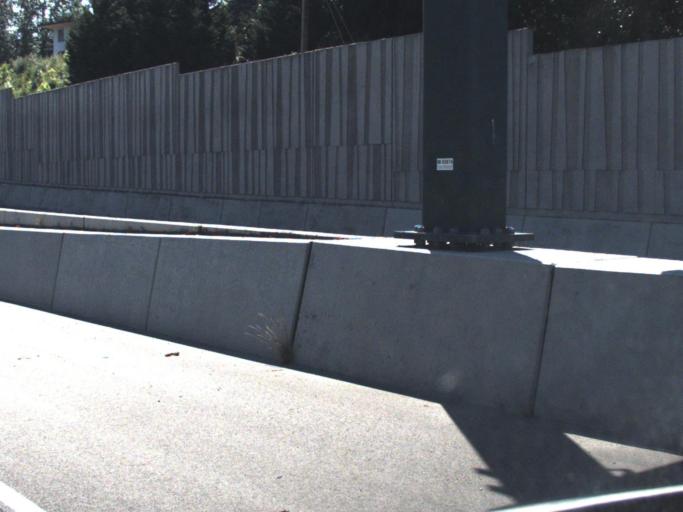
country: US
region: Washington
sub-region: King County
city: Yarrow Point
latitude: 47.6426
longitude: -122.2040
